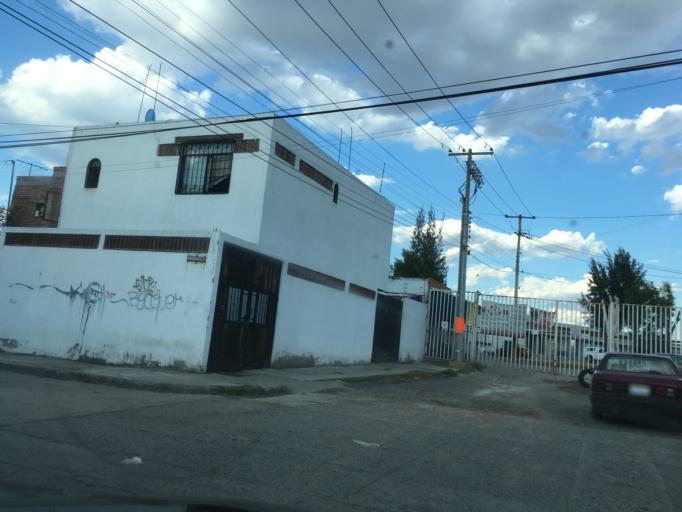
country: MX
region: Guanajuato
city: Leon
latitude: 21.0957
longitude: -101.6379
